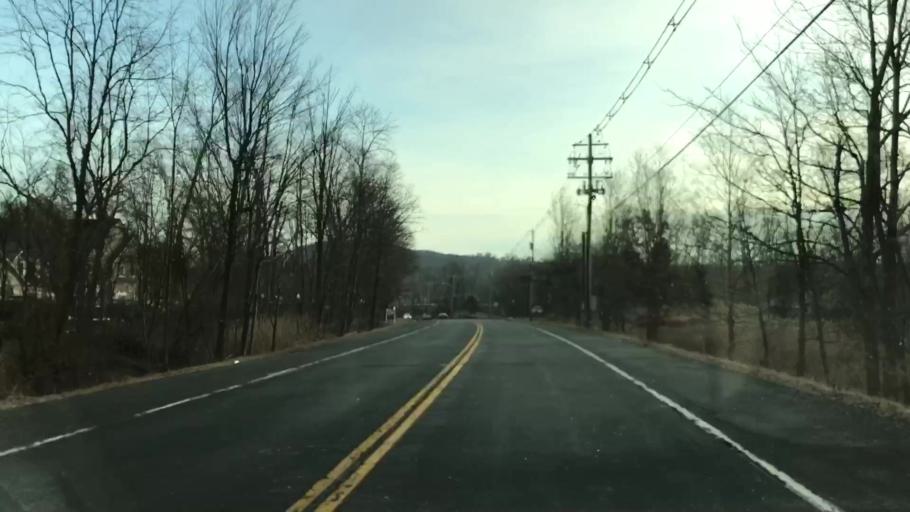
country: US
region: New York
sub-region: Rockland County
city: Pomona
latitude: 41.1821
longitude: -74.0540
